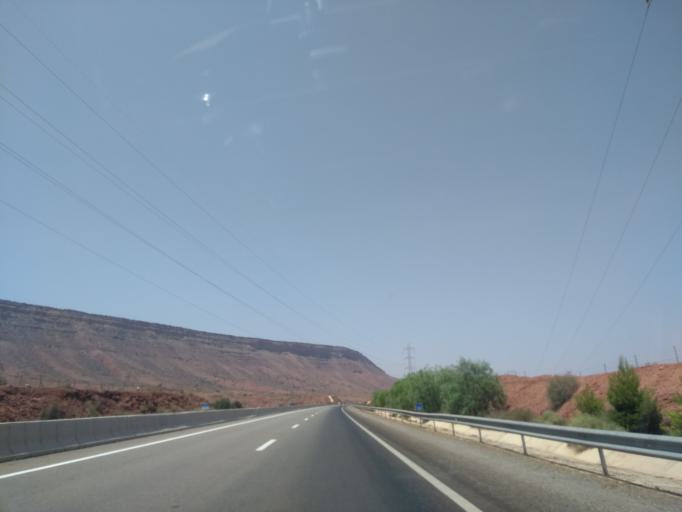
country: MA
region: Marrakech-Tensift-Al Haouz
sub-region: Chichaoua
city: Timezgadiouine
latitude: 30.9198
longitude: -9.0707
